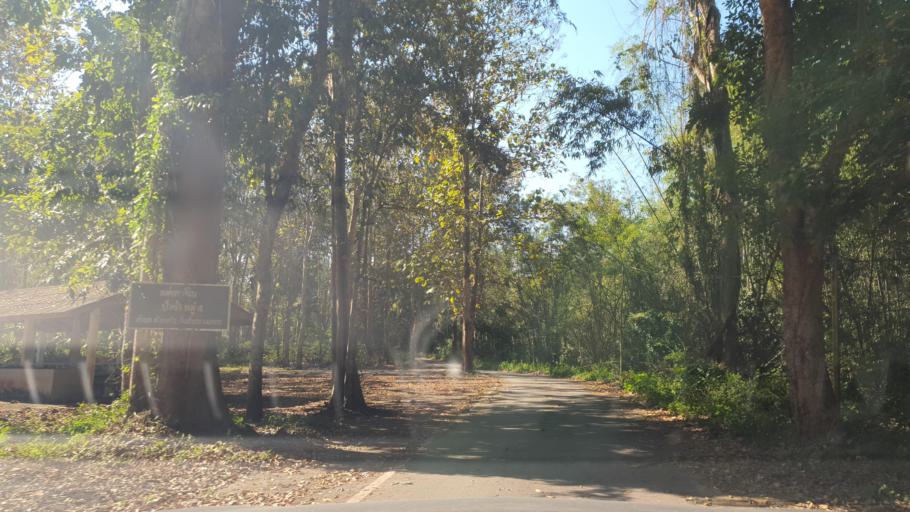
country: TH
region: Chiang Mai
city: Mae On
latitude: 18.8744
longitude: 99.2612
